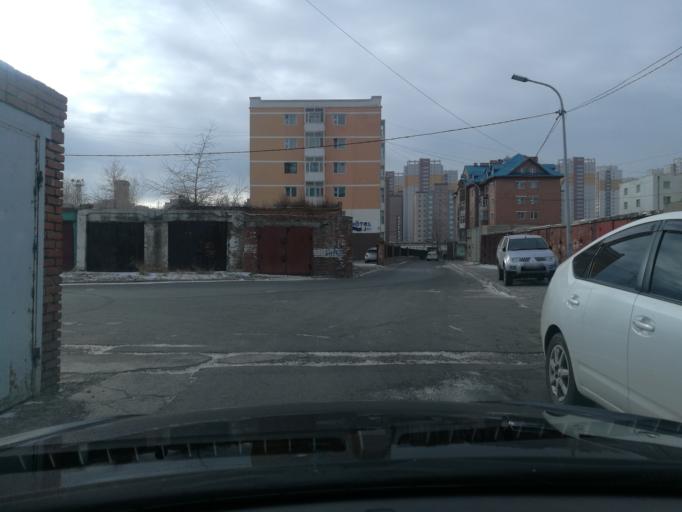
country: MN
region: Ulaanbaatar
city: Ulaanbaatar
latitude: 47.9103
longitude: 106.8996
